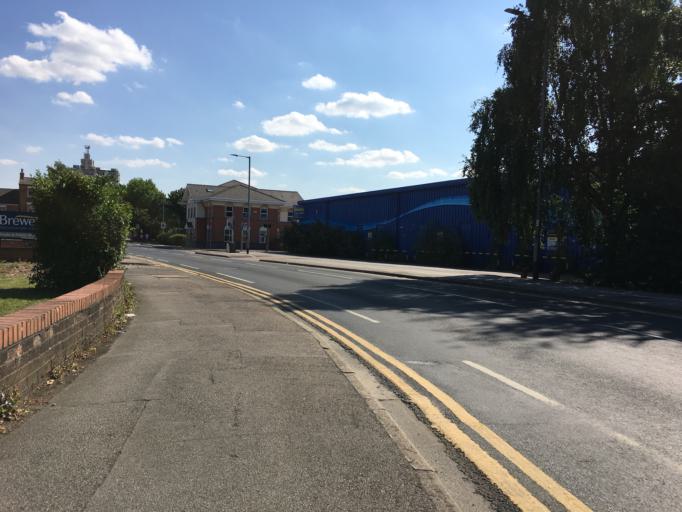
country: GB
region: England
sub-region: City of Kingston upon Hull
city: Hull
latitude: 53.7500
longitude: -0.3407
